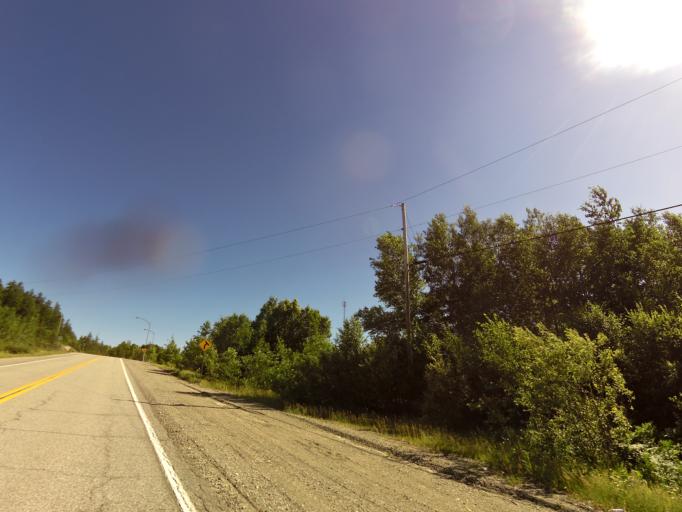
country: CA
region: Quebec
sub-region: Abitibi-Temiscamingue
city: Senneterre
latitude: 48.0950
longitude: -77.3974
